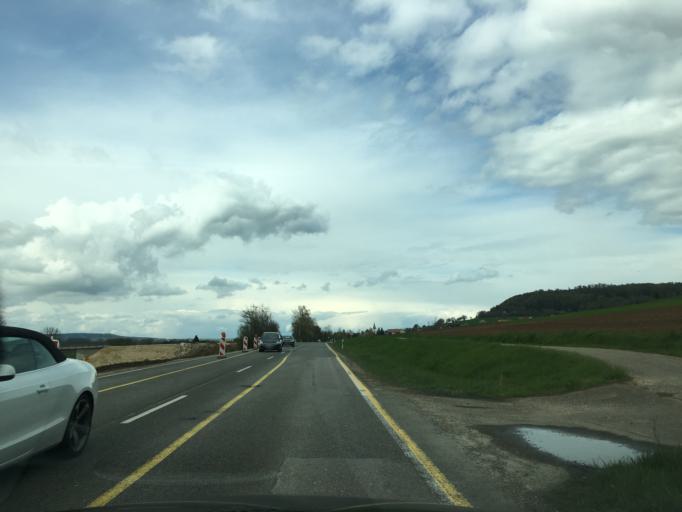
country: DE
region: Bavaria
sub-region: Regierungsbezirk Mittelfranken
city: Treuchtlingen
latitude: 48.9767
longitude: 10.9455
